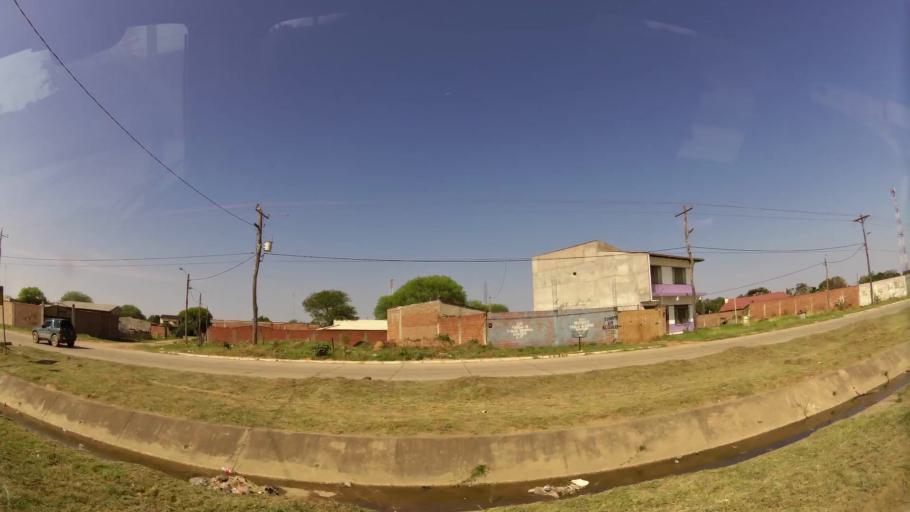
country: BO
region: Santa Cruz
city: Cotoca
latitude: -17.7791
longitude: -63.1079
